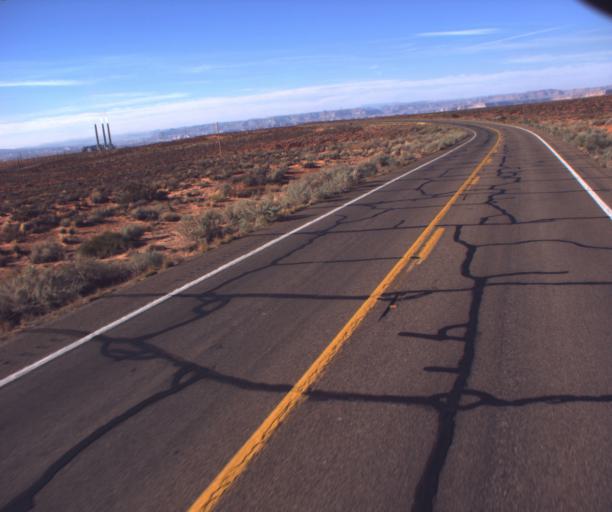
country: US
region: Arizona
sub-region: Coconino County
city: LeChee
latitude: 36.8758
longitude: -111.3432
